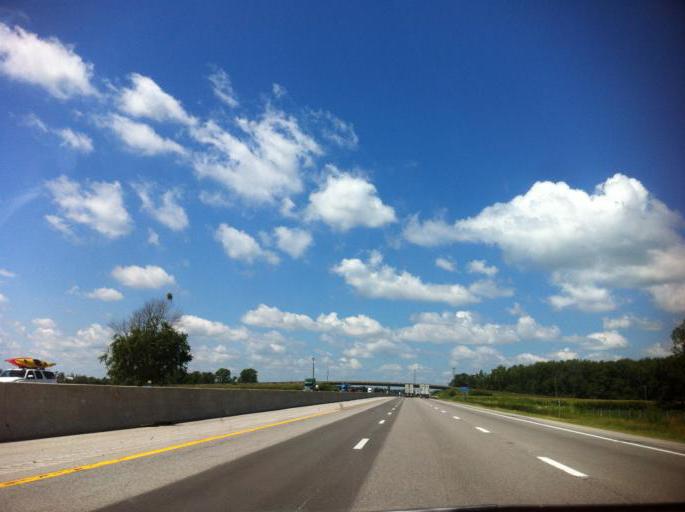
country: US
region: Ohio
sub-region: Ottawa County
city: Elmore
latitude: 41.4403
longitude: -83.2363
